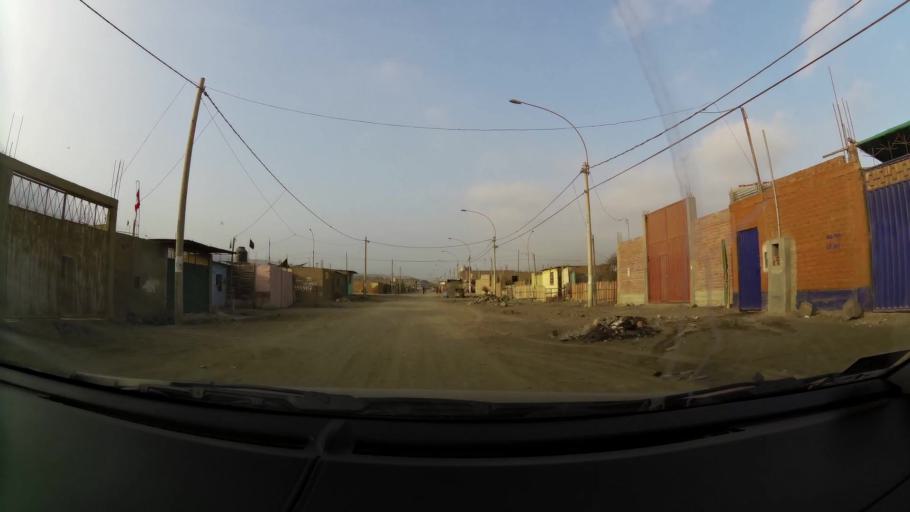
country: PE
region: Lima
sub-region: Lima
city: Santa Rosa
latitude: -11.7437
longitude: -77.1468
